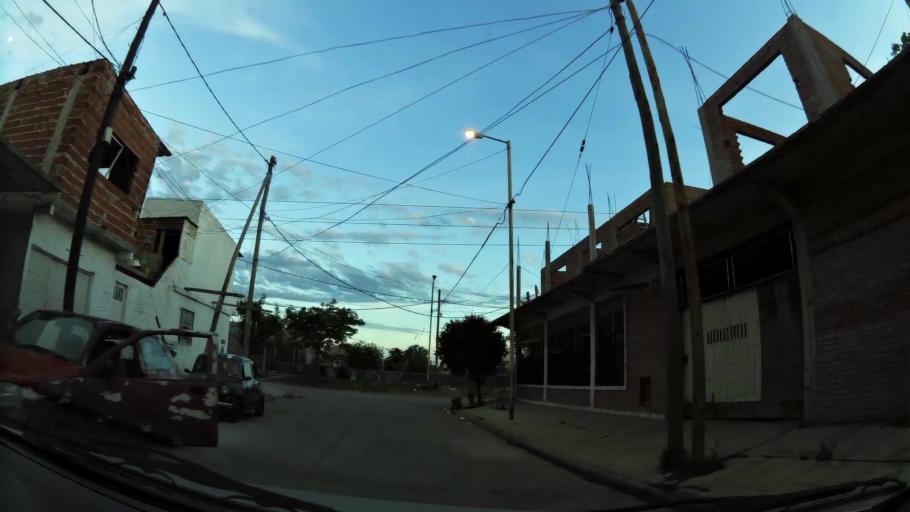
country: AR
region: Buenos Aires
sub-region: Partido de Avellaneda
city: Avellaneda
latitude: -34.6850
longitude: -58.3213
